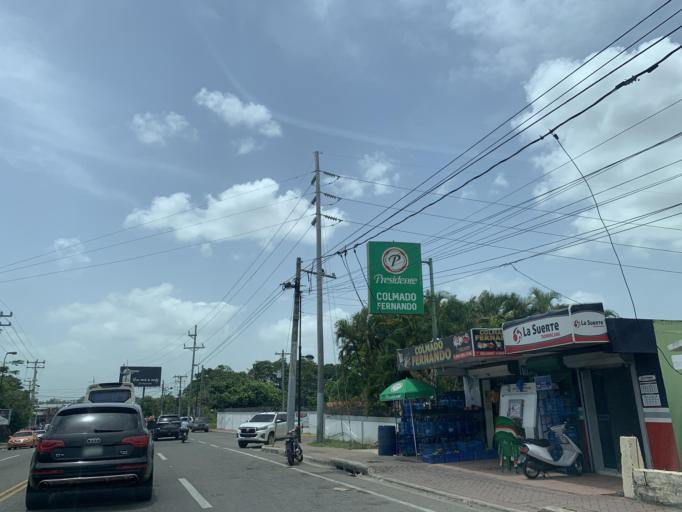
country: DO
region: Puerto Plata
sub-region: Puerto Plata
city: Puerto Plata
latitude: 19.7779
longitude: -70.6679
